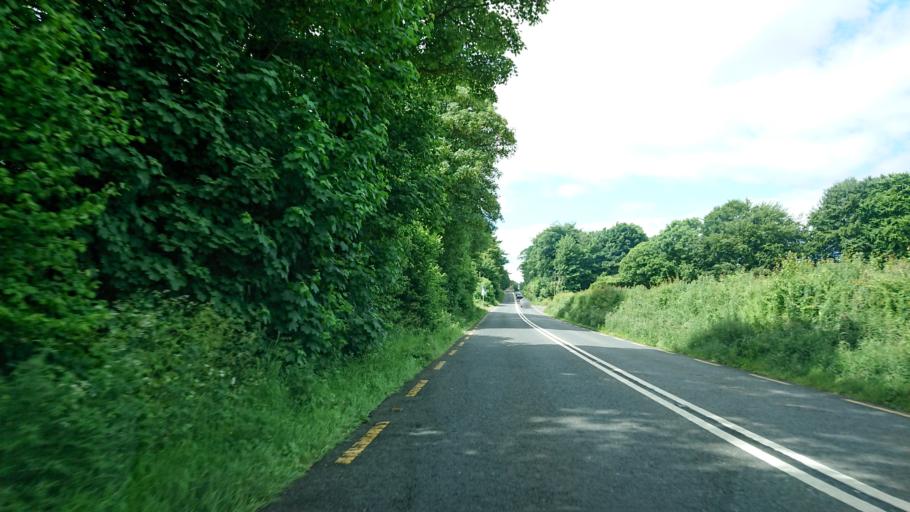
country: IE
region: Leinster
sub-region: Kilkenny
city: Mooncoin
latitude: 52.2305
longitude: -7.2234
